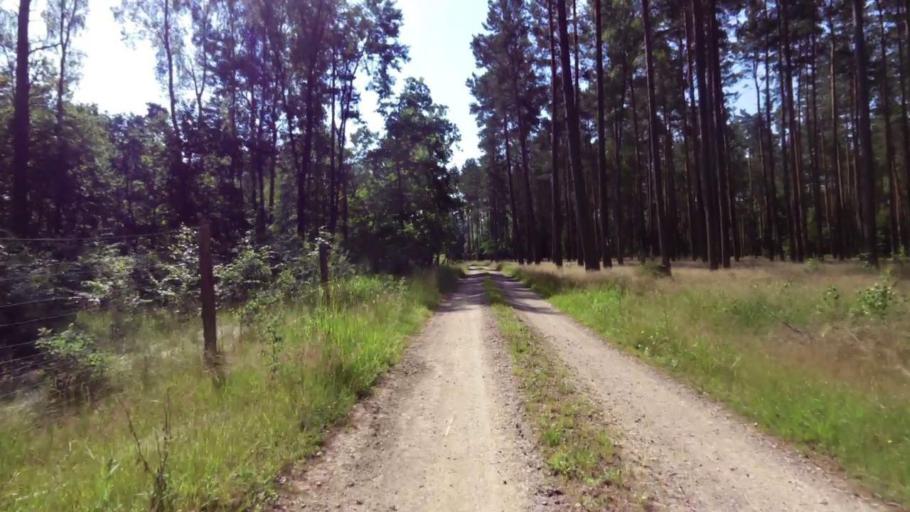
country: PL
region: West Pomeranian Voivodeship
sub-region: Powiat swidwinski
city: Polczyn-Zdroj
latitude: 53.8530
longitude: 16.1389
